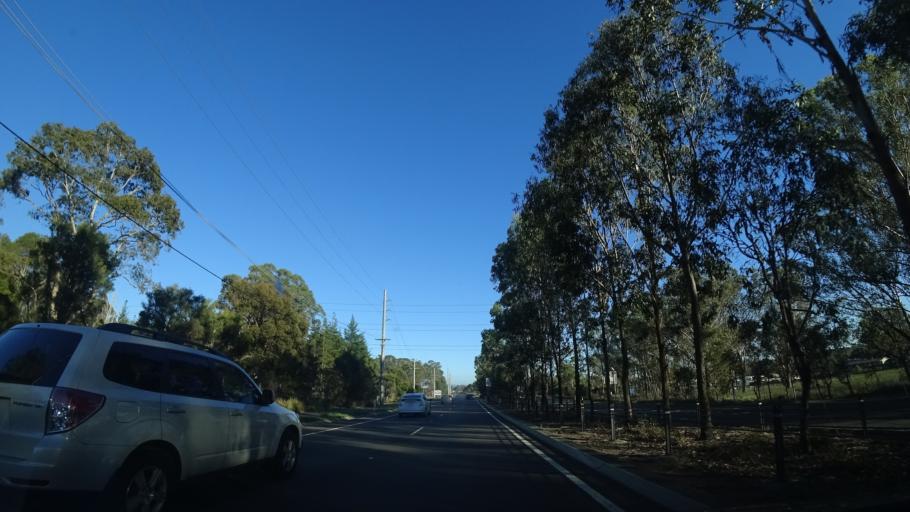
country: AU
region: New South Wales
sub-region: Blacktown
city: Riverstone
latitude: -33.6452
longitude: 150.8575
